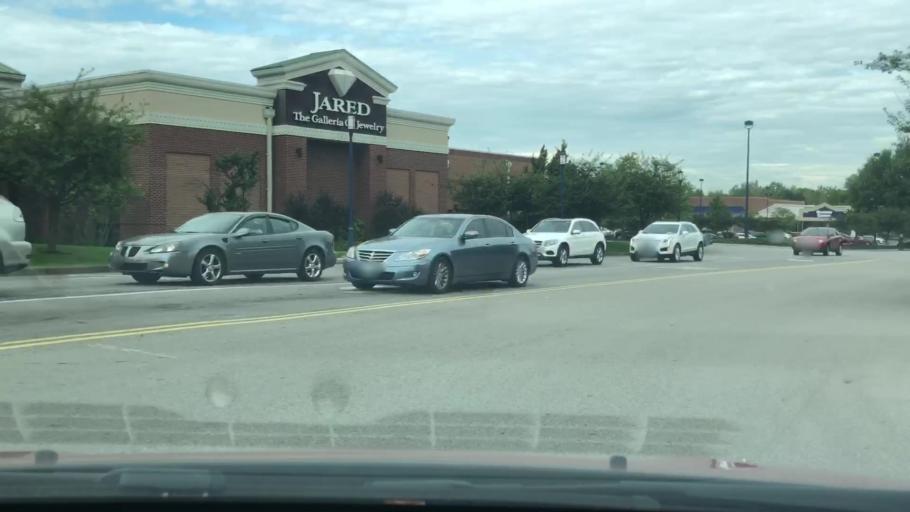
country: US
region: Ohio
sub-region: Franklin County
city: Minerva Park
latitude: 40.0555
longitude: -82.9187
